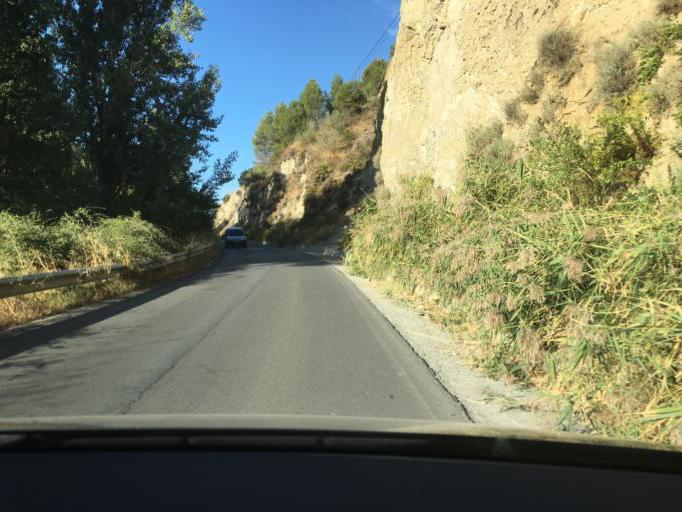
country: ES
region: Andalusia
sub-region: Provincia de Granada
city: Dudar
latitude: 37.1887
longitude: -3.4784
